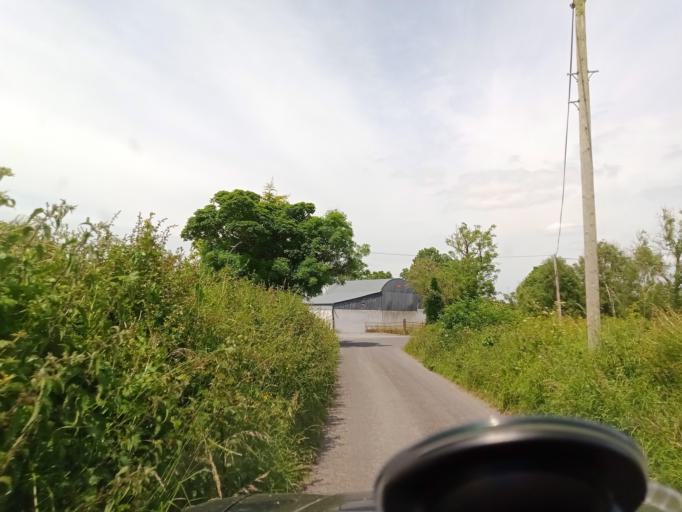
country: IE
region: Leinster
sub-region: Kilkenny
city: Thomastown
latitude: 52.5633
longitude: -7.1021
